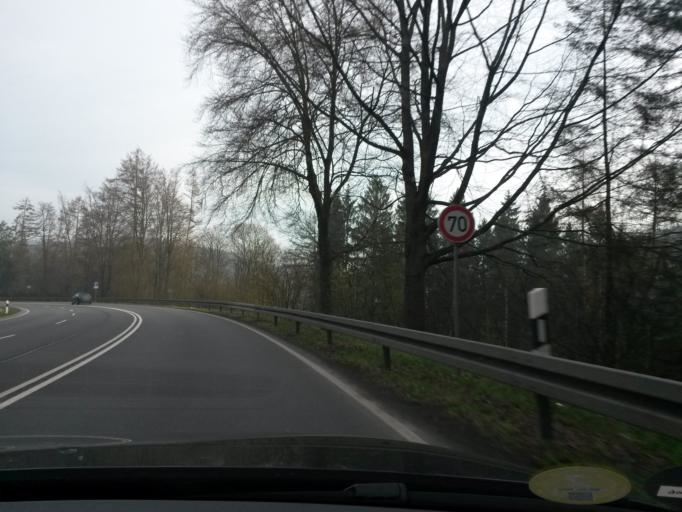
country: DE
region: North Rhine-Westphalia
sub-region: Regierungsbezirk Arnsberg
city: Herscheid
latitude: 51.1929
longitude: 7.6923
